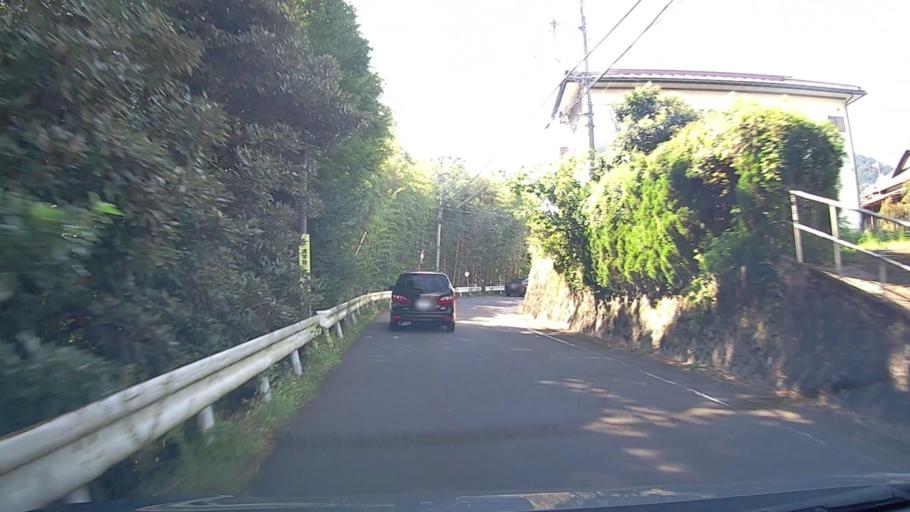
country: JP
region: Kanagawa
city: Odawara
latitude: 35.3459
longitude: 139.0812
